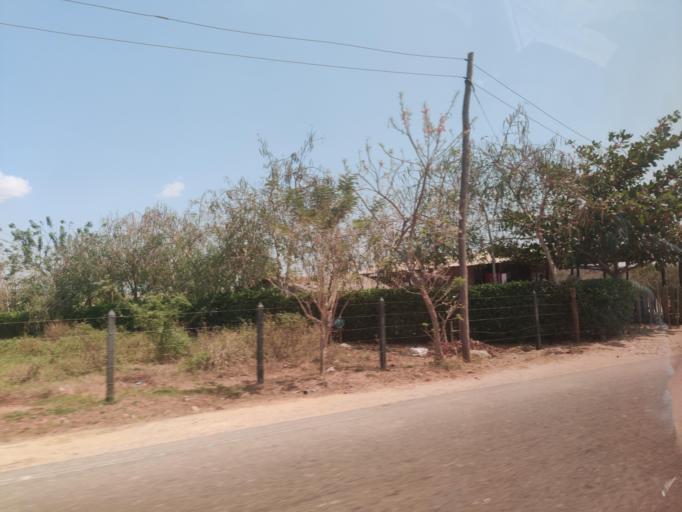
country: CO
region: Bolivar
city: Turbana
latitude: 10.2756
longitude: -75.5119
